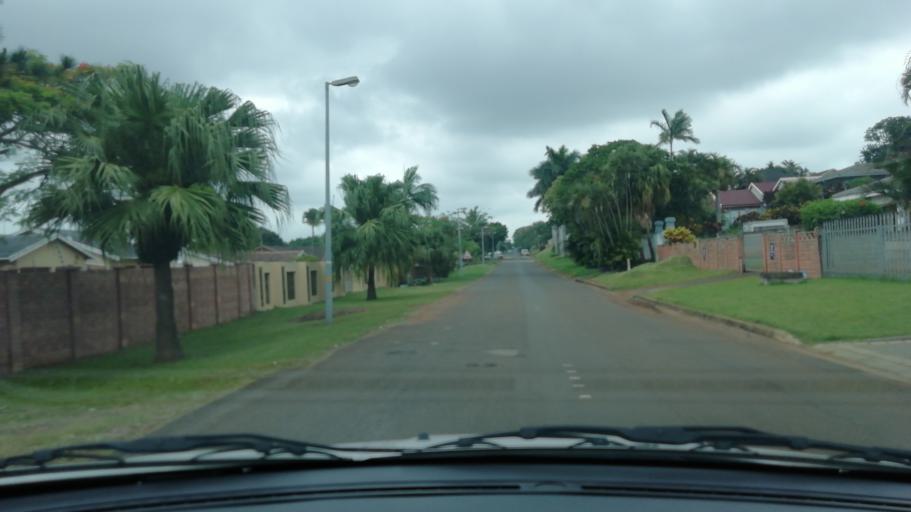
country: ZA
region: KwaZulu-Natal
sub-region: uThungulu District Municipality
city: Empangeni
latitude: -28.7658
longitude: 31.9030
